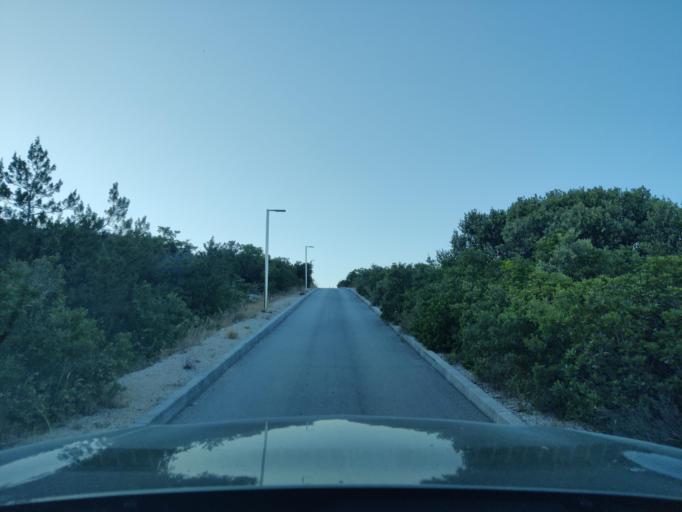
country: HR
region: Sibensko-Kniniska
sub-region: Grad Sibenik
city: Tisno
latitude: 43.8103
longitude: 15.6281
